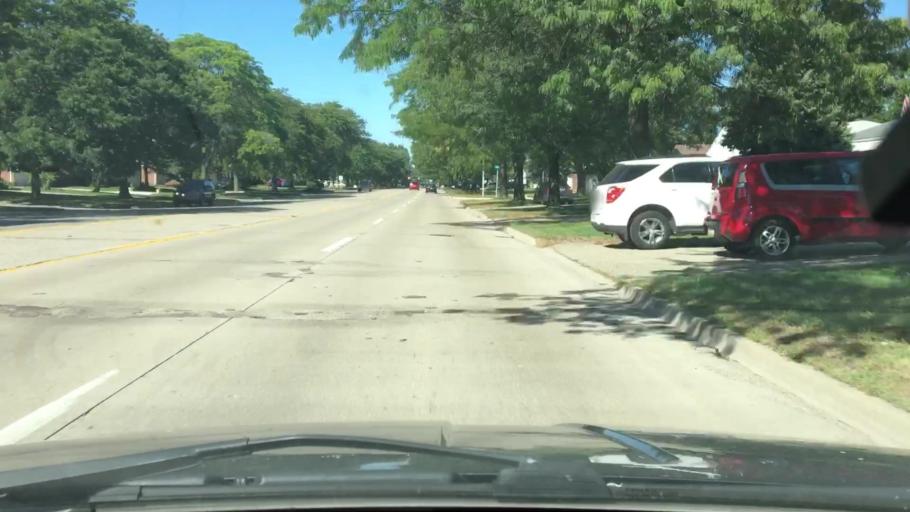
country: US
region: Michigan
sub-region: Wayne County
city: Livonia
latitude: 42.3862
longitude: -83.3534
